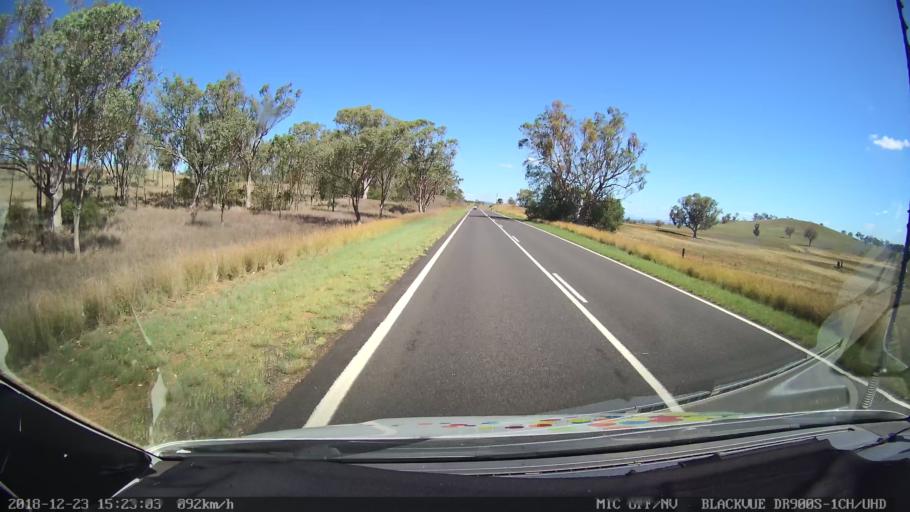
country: AU
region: New South Wales
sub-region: Tamworth Municipality
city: Manilla
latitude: -30.8757
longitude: 150.8105
